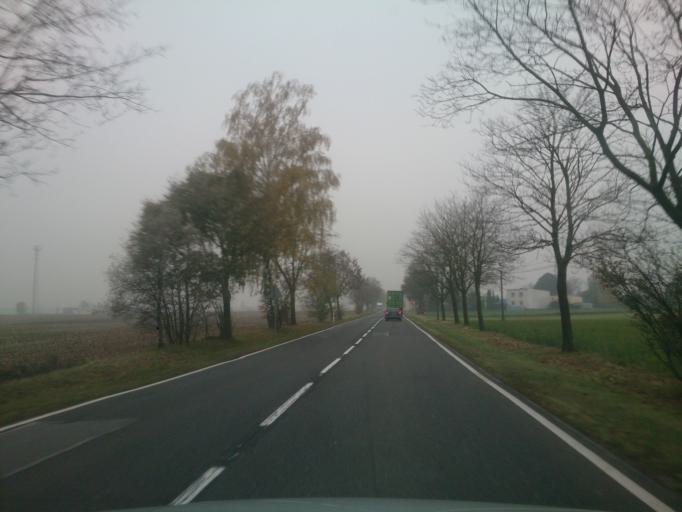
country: PL
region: Kujawsko-Pomorskie
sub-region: Powiat wabrzeski
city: Debowa Laka
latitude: 53.2115
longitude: 19.1766
